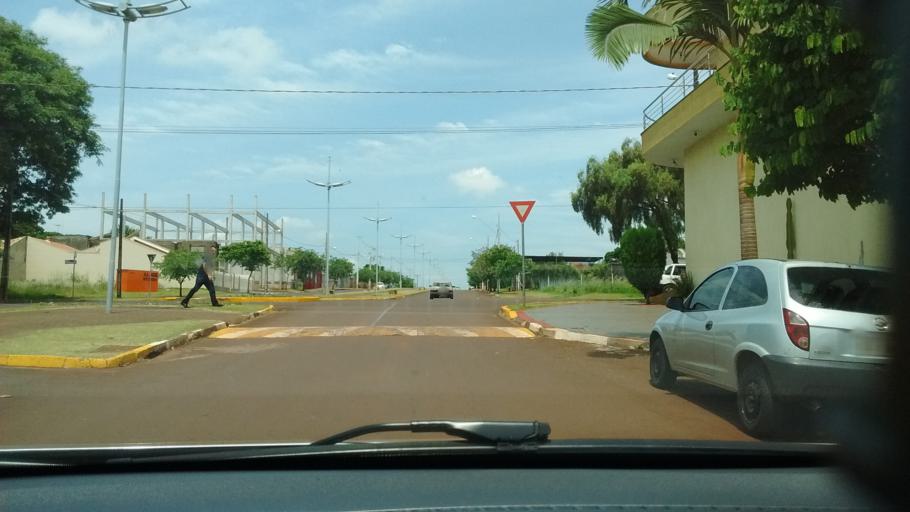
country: BR
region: Parana
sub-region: Corbelia
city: Corbelia
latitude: -24.5503
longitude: -52.9895
